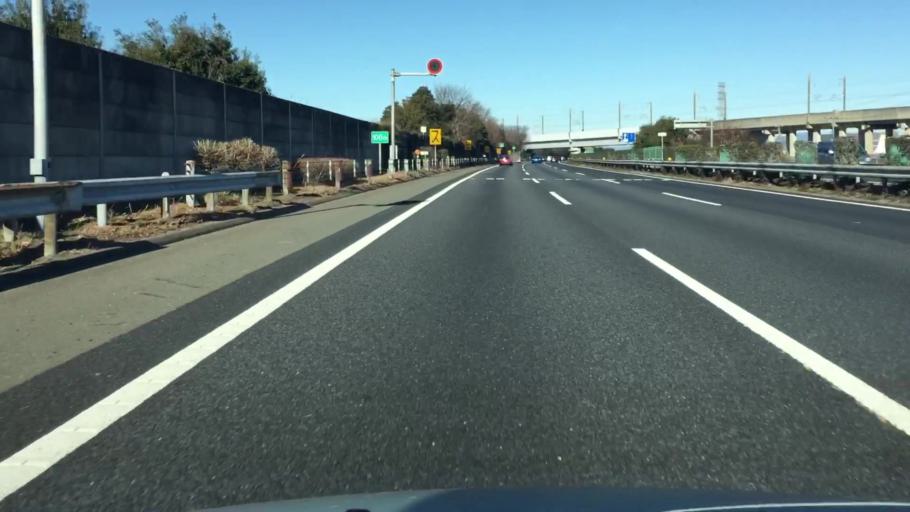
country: JP
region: Saitama
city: Honjo
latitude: 36.2310
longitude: 139.1511
